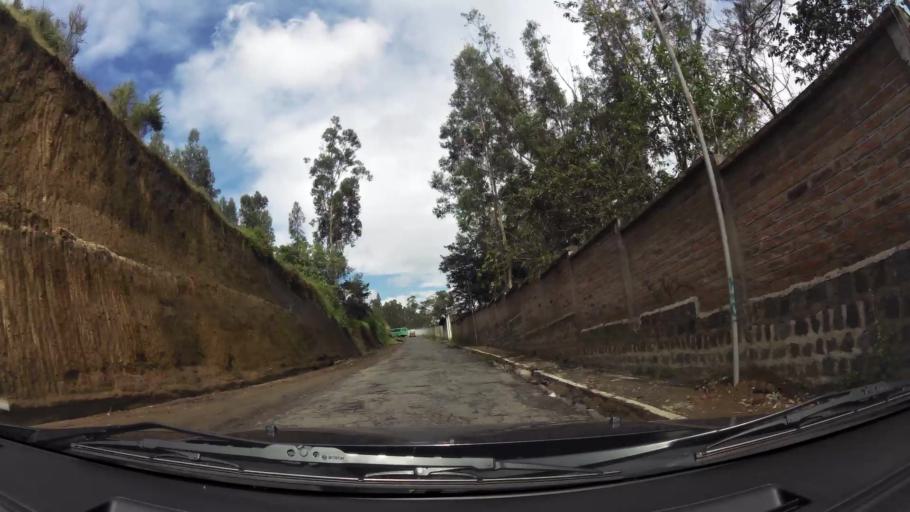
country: EC
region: Pichincha
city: Sangolqui
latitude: -0.3055
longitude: -78.4269
